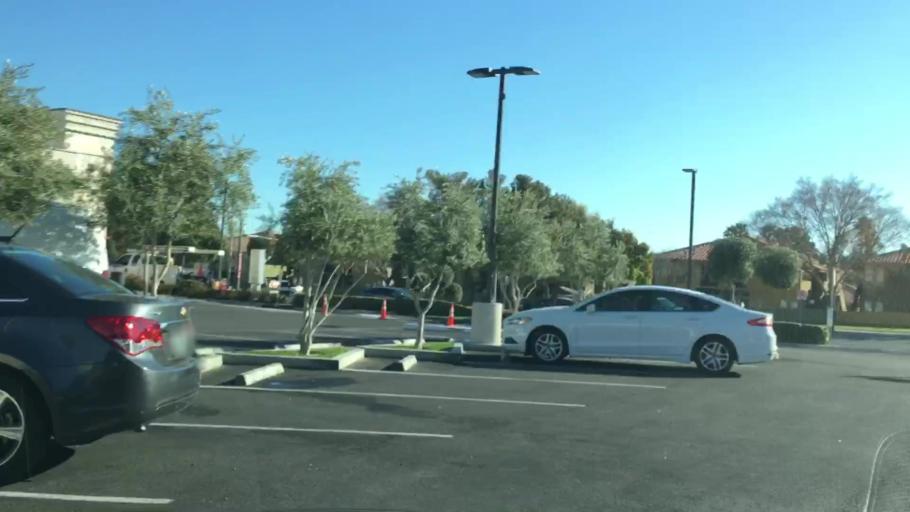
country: US
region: Nevada
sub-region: Clark County
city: Summerlin South
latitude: 36.1449
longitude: -115.3145
